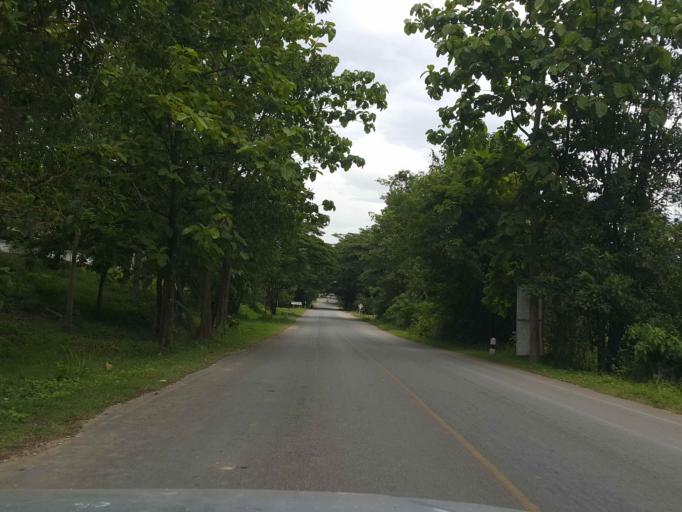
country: TH
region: Lampang
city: Thoen
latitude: 17.5936
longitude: 99.3317
